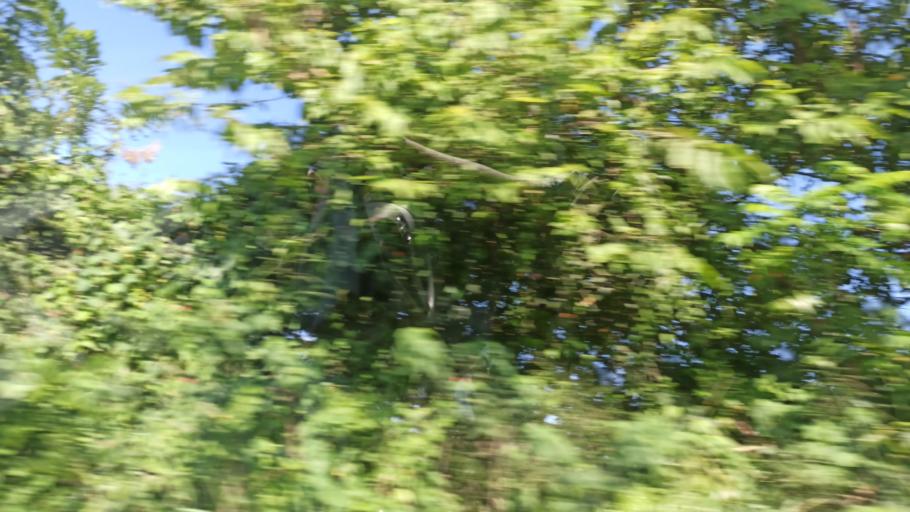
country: MX
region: Veracruz
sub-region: Martinez de la Torre
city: La Union Paso Largo
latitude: 20.1450
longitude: -96.9996
